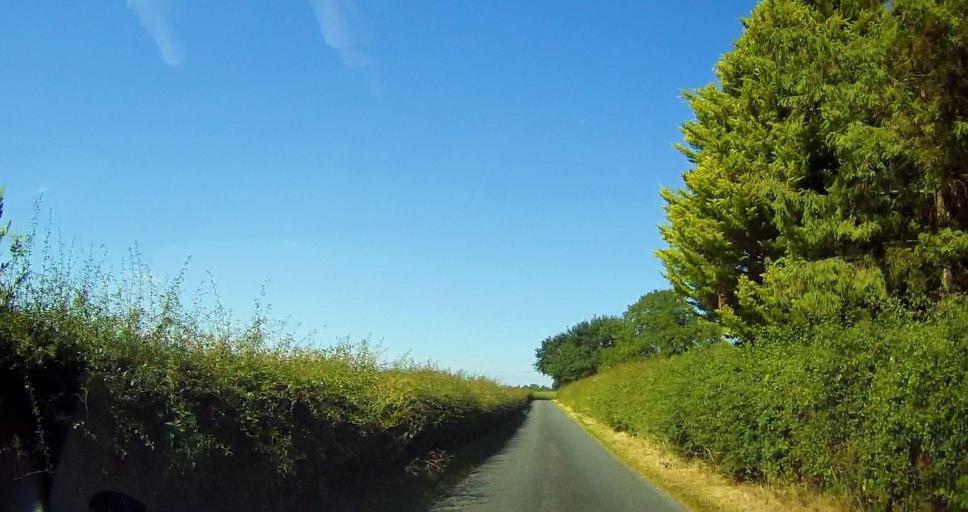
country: GB
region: England
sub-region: Cheshire East
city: Sandbach
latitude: 53.1522
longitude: -2.3575
